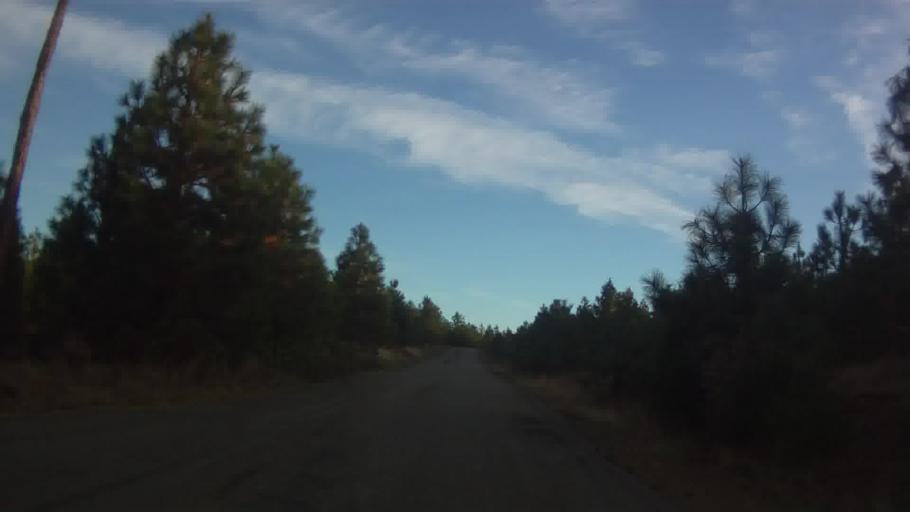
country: US
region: California
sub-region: Shasta County
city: Shingletown
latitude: 40.6296
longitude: -121.8573
